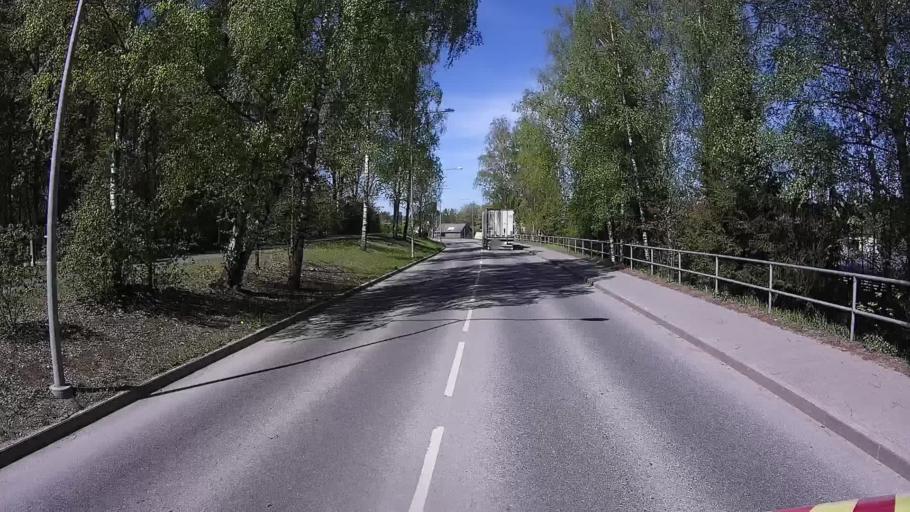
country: EE
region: Vorumaa
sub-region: Voru linn
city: Voru
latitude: 57.8253
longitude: 27.0153
